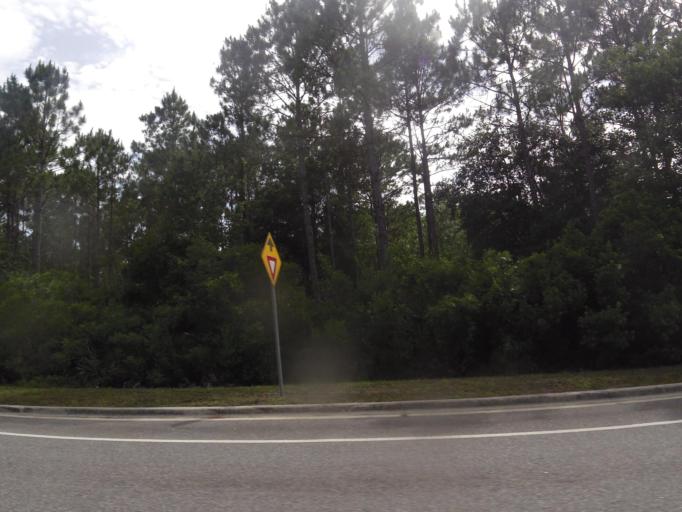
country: US
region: Florida
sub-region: Saint Johns County
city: Saint Augustine
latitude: 29.8985
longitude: -81.3469
